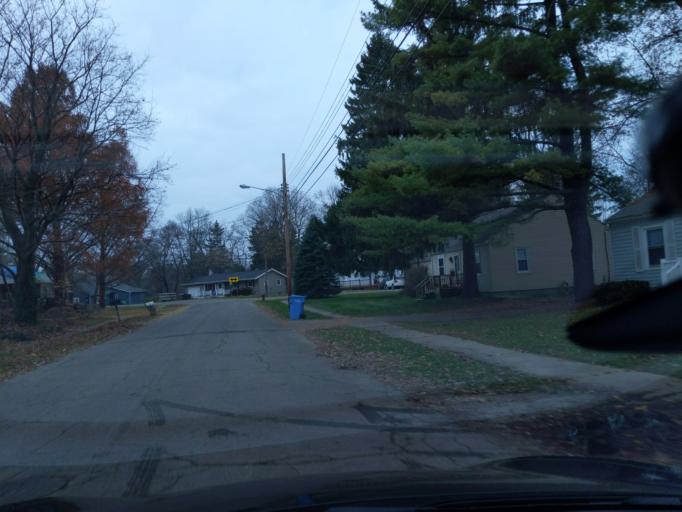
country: US
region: Michigan
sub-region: Ingham County
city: Edgemont Park
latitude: 42.7632
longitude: -84.5744
